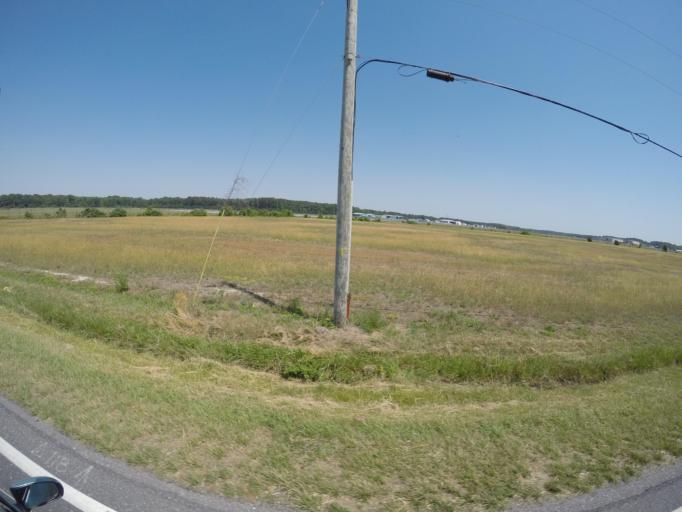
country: US
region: Delaware
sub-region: Sussex County
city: Georgetown
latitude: 38.6816
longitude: -75.3643
